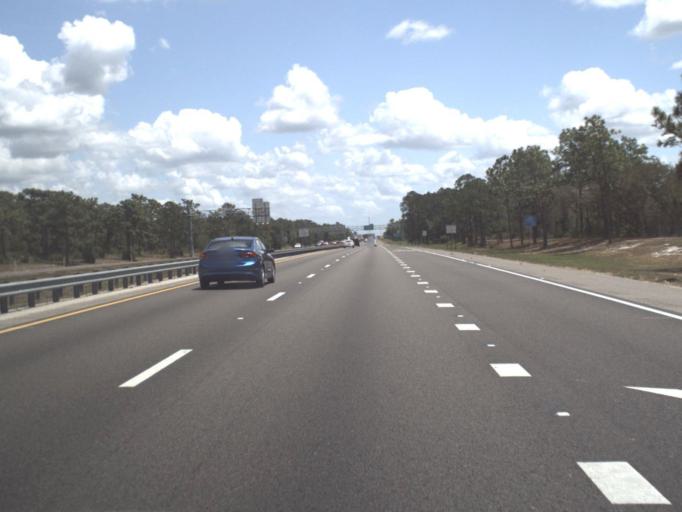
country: US
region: Florida
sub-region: Orange County
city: Alafaya
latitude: 28.4515
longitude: -81.1992
